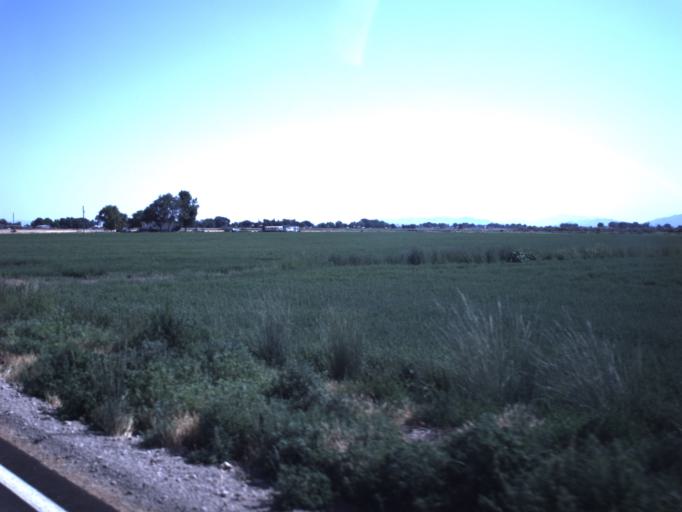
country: US
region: Utah
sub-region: Millard County
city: Delta
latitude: 39.2735
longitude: -112.6530
